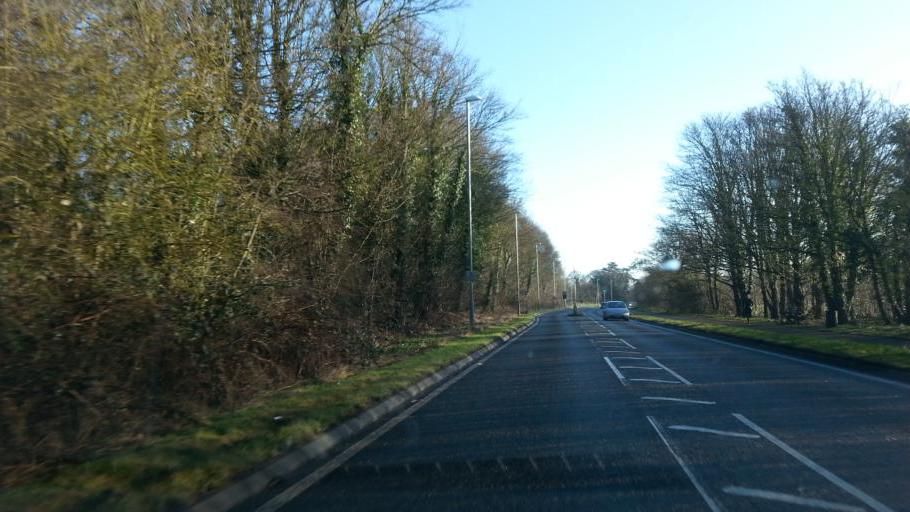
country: GB
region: England
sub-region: Nottinghamshire
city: South Collingham
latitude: 53.0797
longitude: -0.7642
